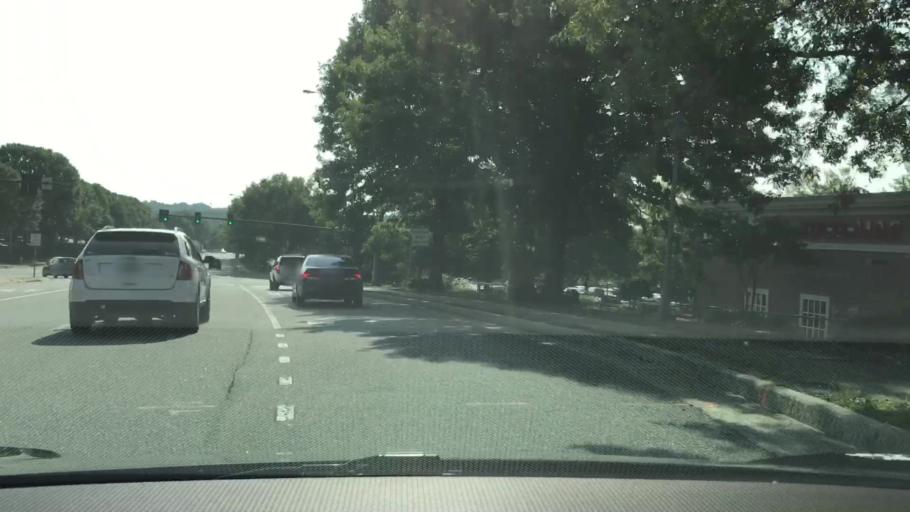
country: US
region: Georgia
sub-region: Gwinnett County
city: Buford
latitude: 34.0686
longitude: -83.9842
